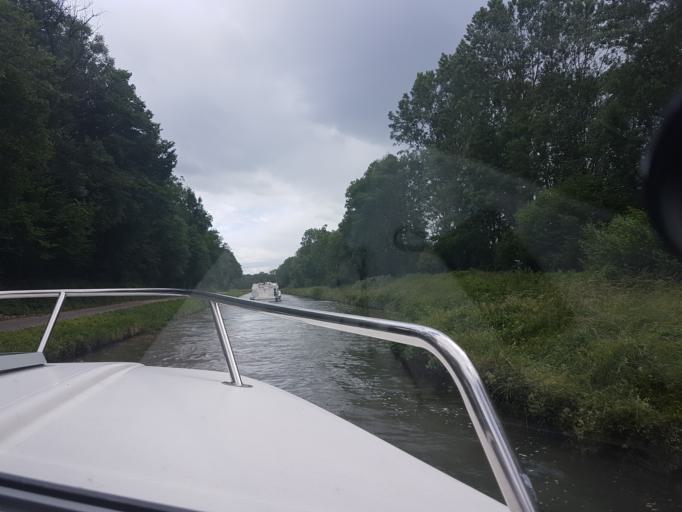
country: FR
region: Bourgogne
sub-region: Departement de l'Yonne
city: Vermenton
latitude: 47.5543
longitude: 3.6328
